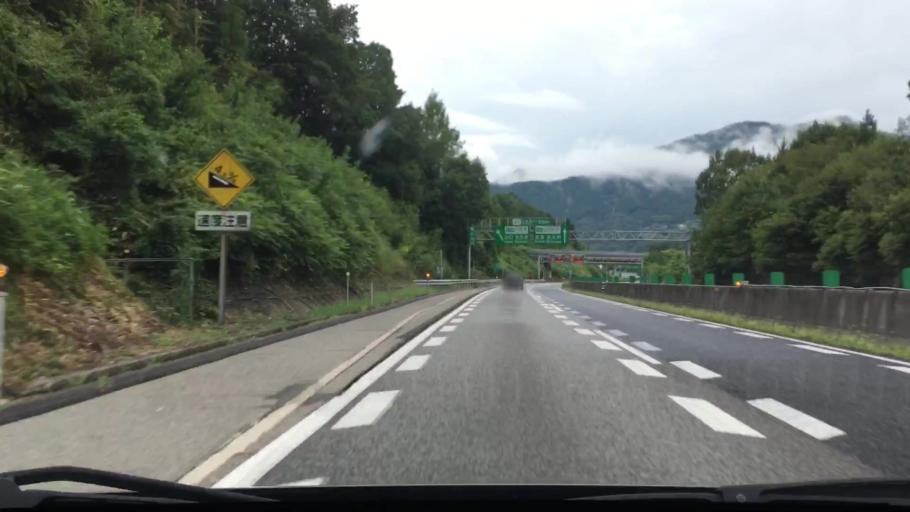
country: JP
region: Hiroshima
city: Hiroshima-shi
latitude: 34.5799
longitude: 132.4657
